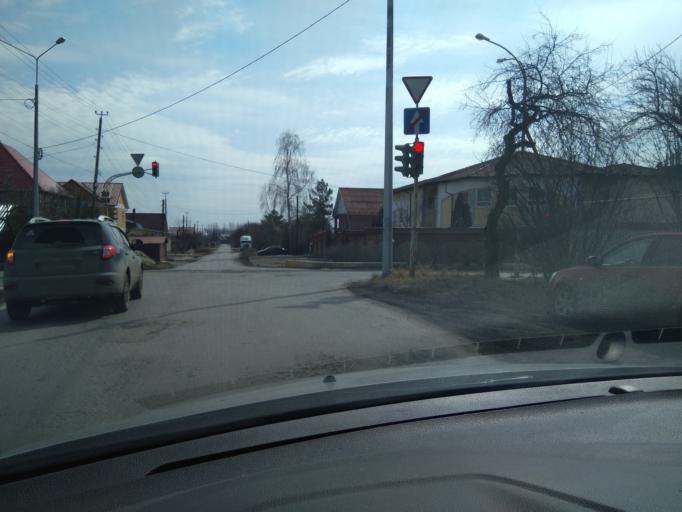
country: RU
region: Sverdlovsk
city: Shuvakish
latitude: 56.8907
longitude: 60.4851
